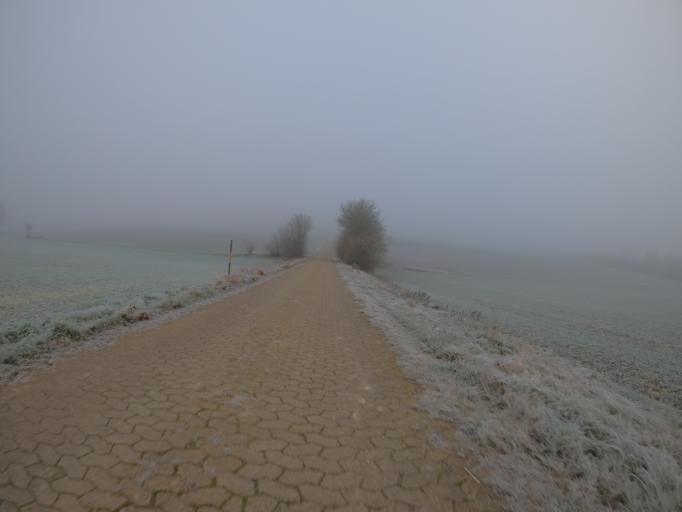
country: DE
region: Baden-Wuerttemberg
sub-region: Tuebingen Region
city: Beimerstetten
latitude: 48.4850
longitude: 9.9737
